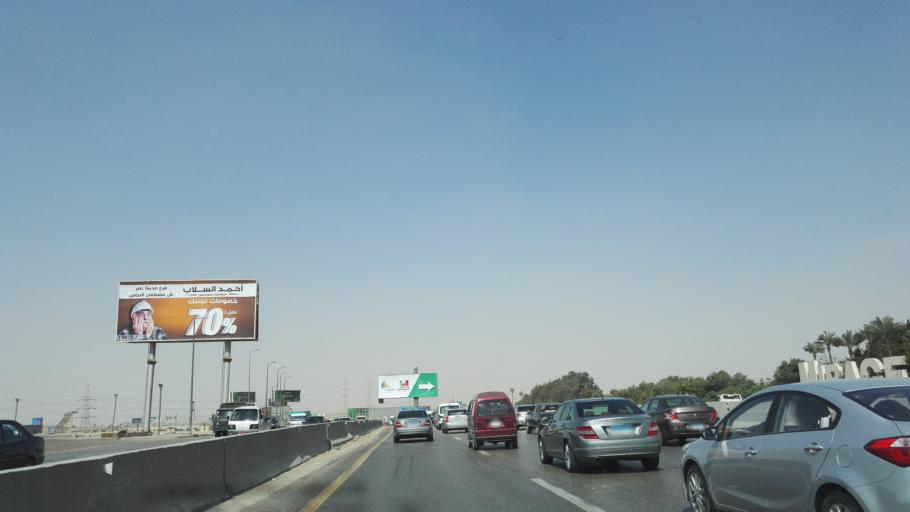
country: EG
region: Muhafazat al Qalyubiyah
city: Al Khankah
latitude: 30.0727
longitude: 31.4306
